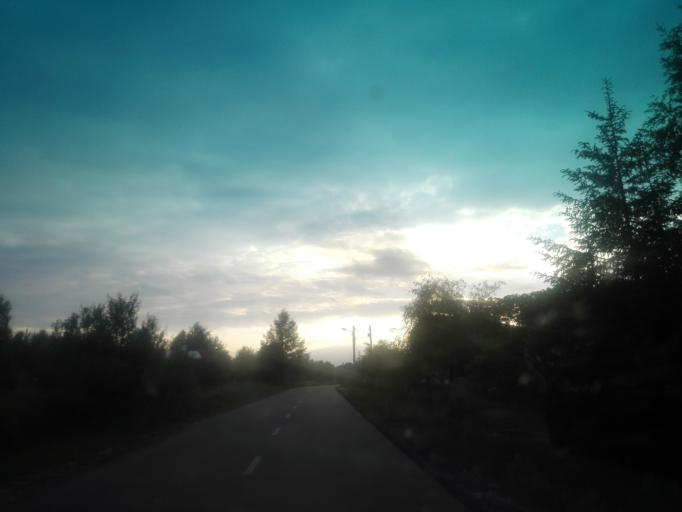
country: PL
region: Silesian Voivodeship
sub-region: Powiat czestochowski
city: Potok Zloty
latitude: 50.6932
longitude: 19.3860
